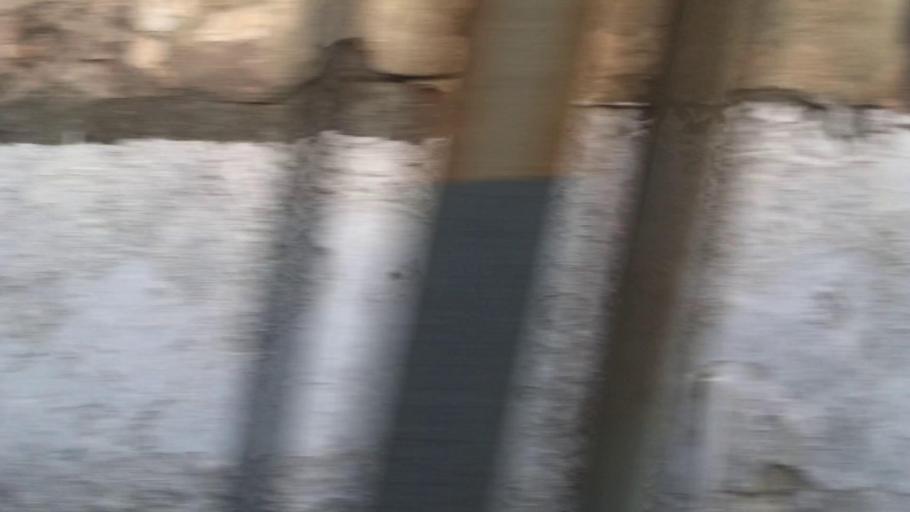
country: BR
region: Rio de Janeiro
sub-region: Rio De Janeiro
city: Rio de Janeiro
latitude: -22.9014
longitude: -43.2566
